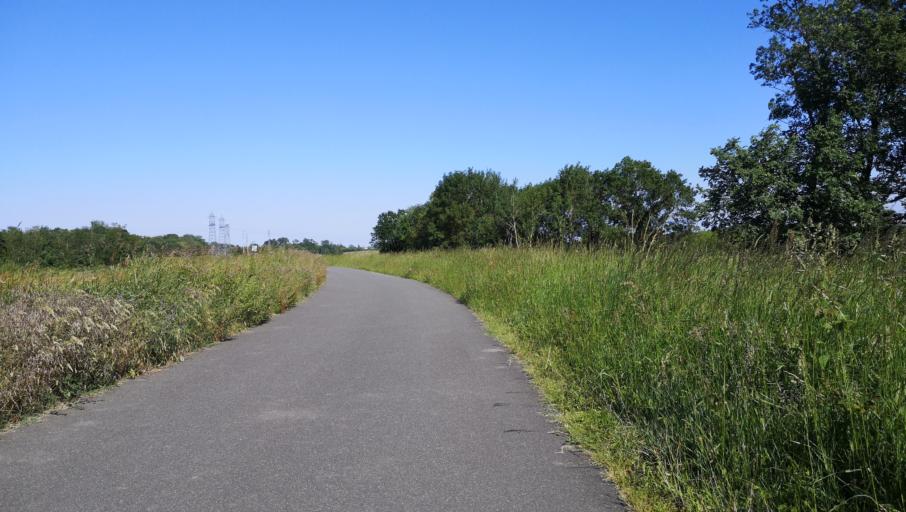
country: FR
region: Centre
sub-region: Departement du Loiret
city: Mareau-aux-Pres
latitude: 47.8620
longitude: 1.8014
